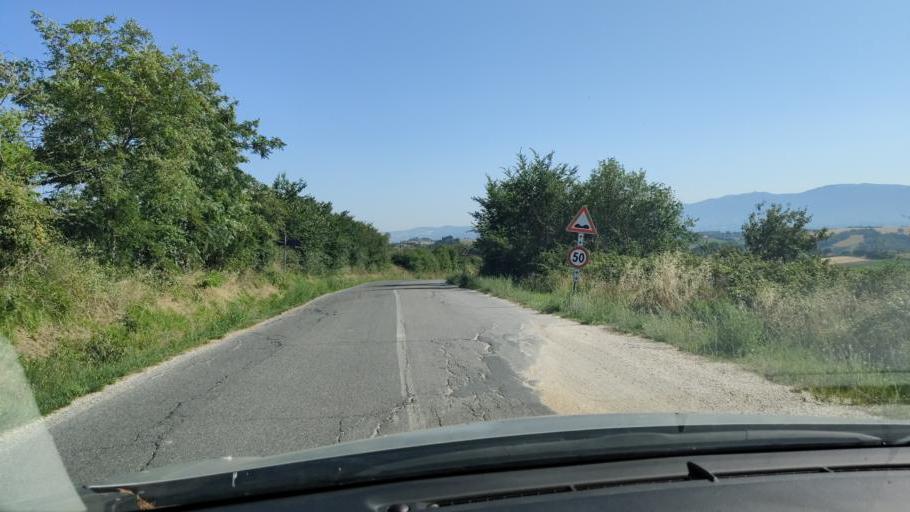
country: IT
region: Umbria
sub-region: Provincia di Terni
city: Avigliano Umbro
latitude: 42.6750
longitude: 12.4405
